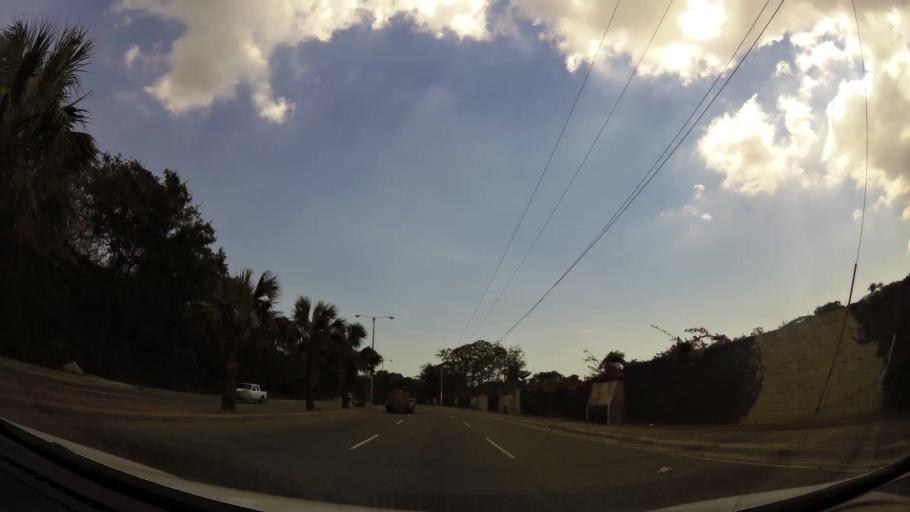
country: DO
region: Nacional
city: La Agustina
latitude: 18.5307
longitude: -69.9546
